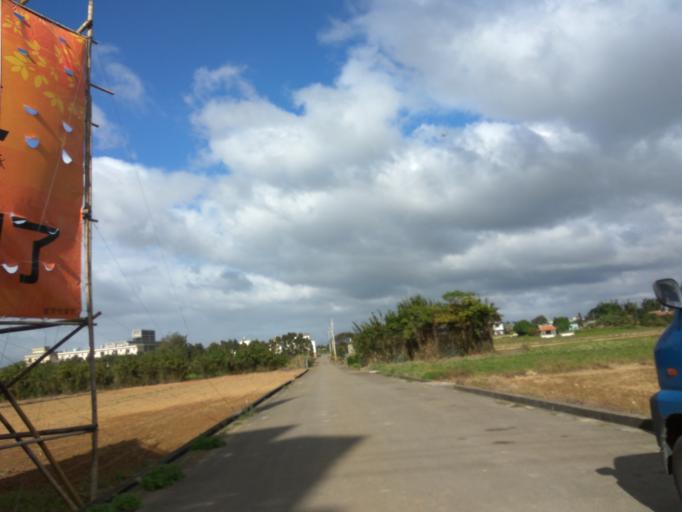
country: TW
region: Taiwan
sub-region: Hsinchu
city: Zhubei
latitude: 24.9691
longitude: 121.0880
